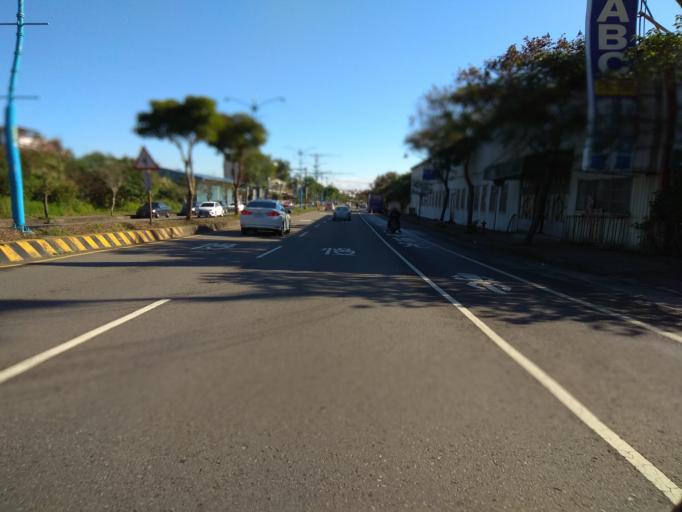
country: TW
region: Taiwan
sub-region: Hsinchu
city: Zhubei
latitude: 24.9060
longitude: 121.1329
